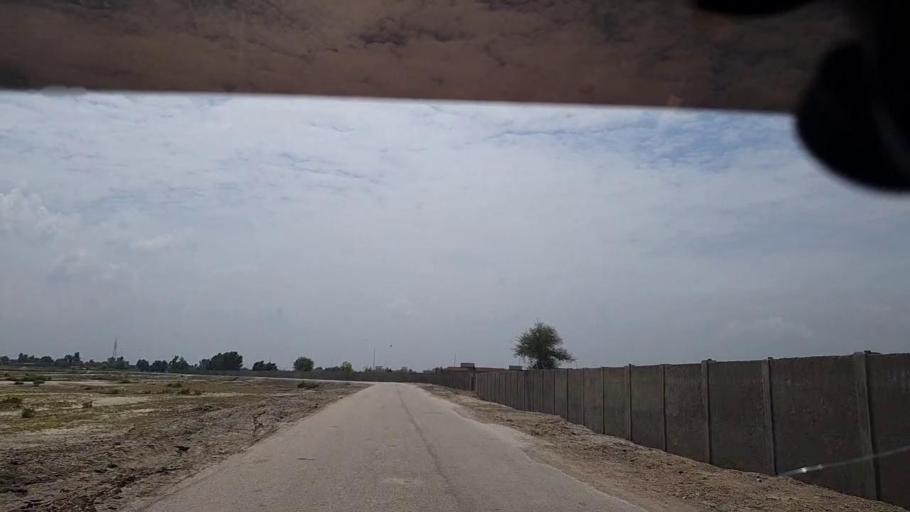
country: PK
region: Sindh
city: Ghauspur
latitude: 28.0939
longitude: 68.9595
